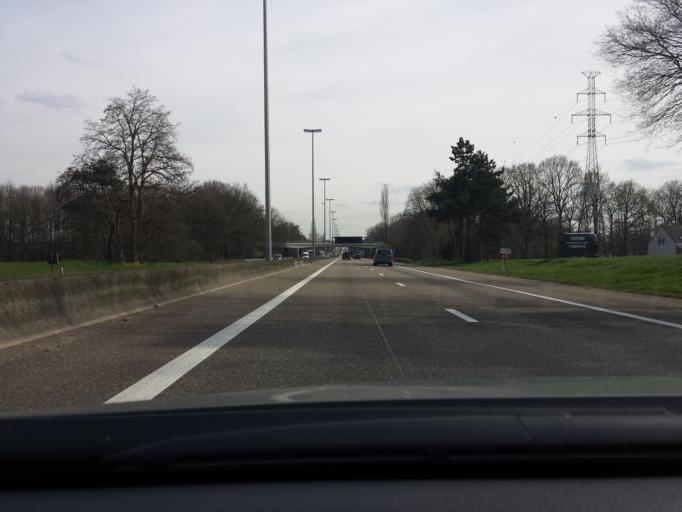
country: BE
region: Flanders
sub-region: Provincie Limburg
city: Beringen
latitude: 51.0253
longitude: 5.2039
